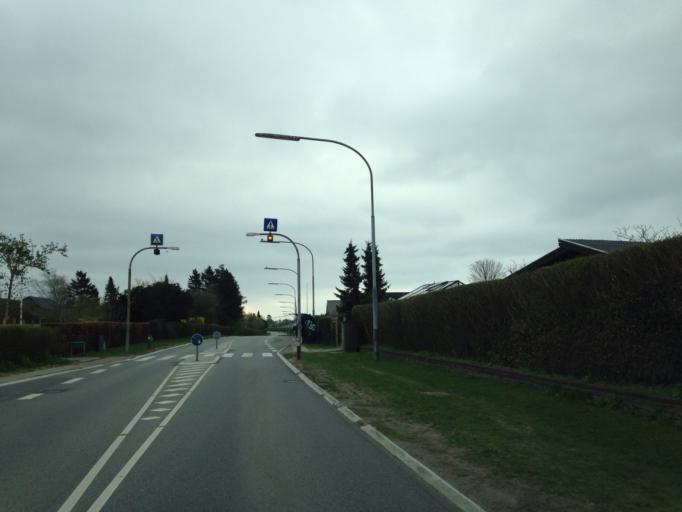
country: DK
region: Zealand
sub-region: Greve Kommune
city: Greve
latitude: 55.5963
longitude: 12.3084
